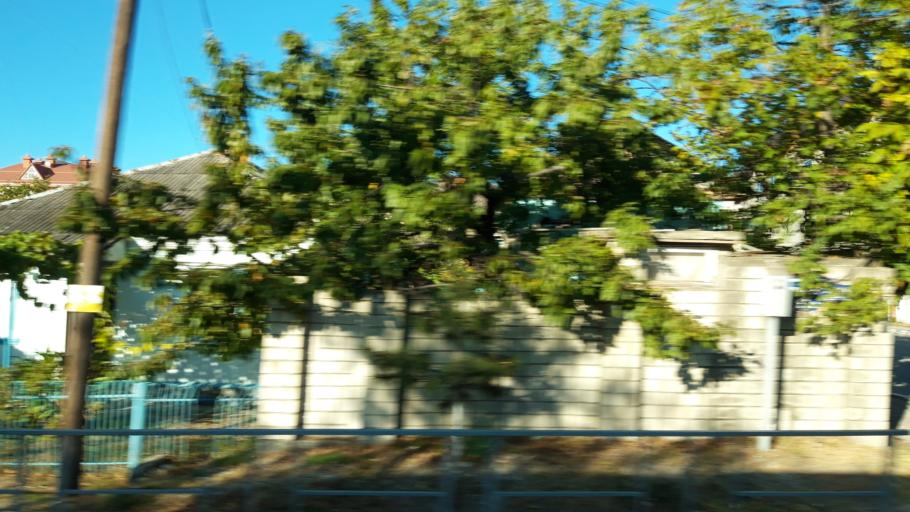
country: RU
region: Krasnodarskiy
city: Kabardinka
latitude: 44.6485
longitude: 37.9483
